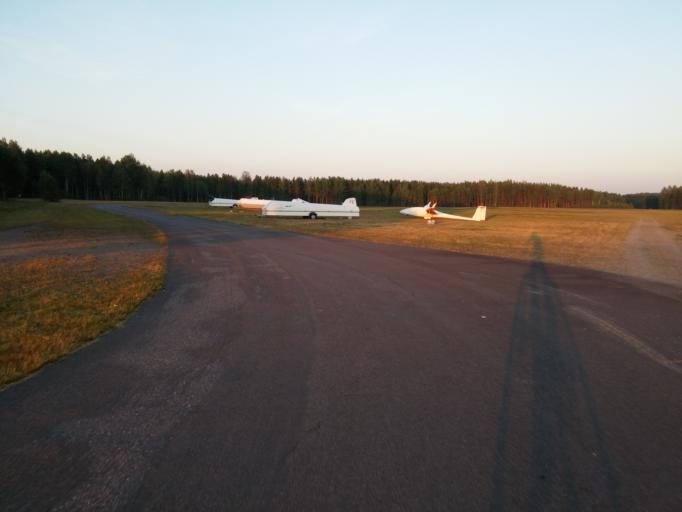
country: FI
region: Uusimaa
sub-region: Helsinki
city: Kaerkoelae
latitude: 60.7445
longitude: 24.1160
